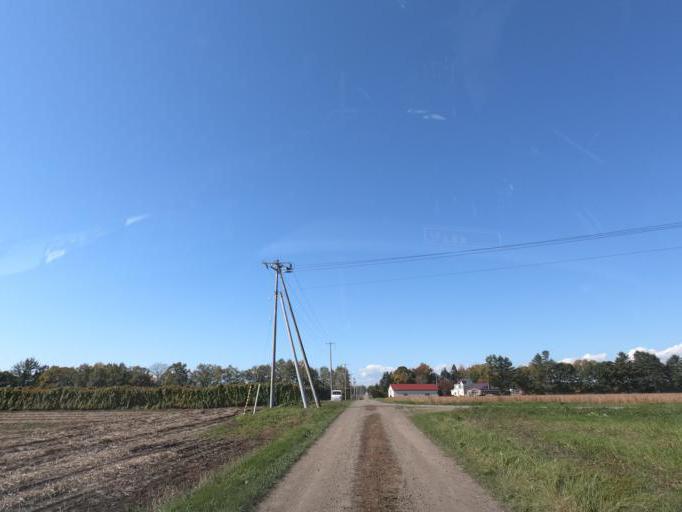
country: JP
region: Hokkaido
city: Otofuke
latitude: 43.0646
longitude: 143.2760
